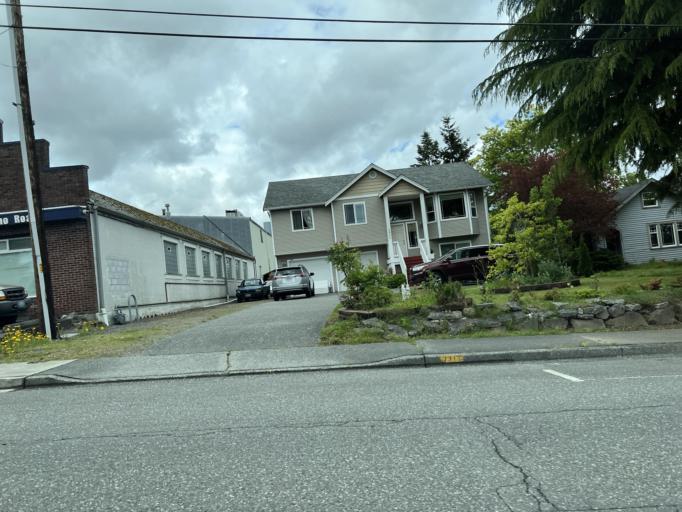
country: US
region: Washington
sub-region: Snohomish County
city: Everett
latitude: 47.9261
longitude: -122.2147
